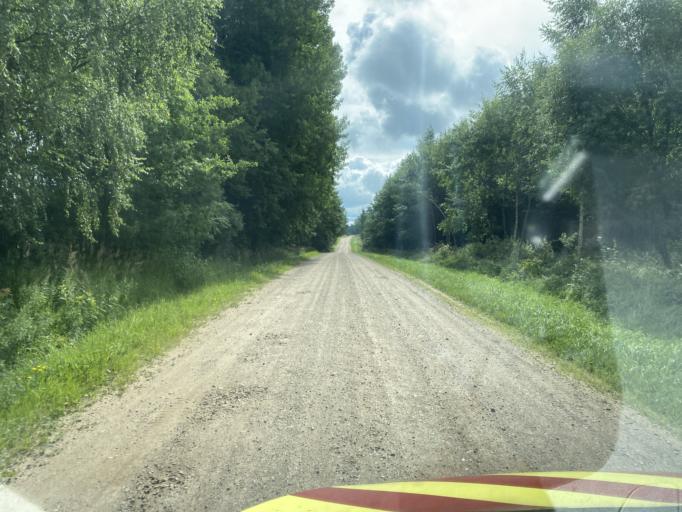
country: EE
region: Viljandimaa
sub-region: Karksi vald
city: Karksi-Nuia
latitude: 58.0846
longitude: 25.5051
